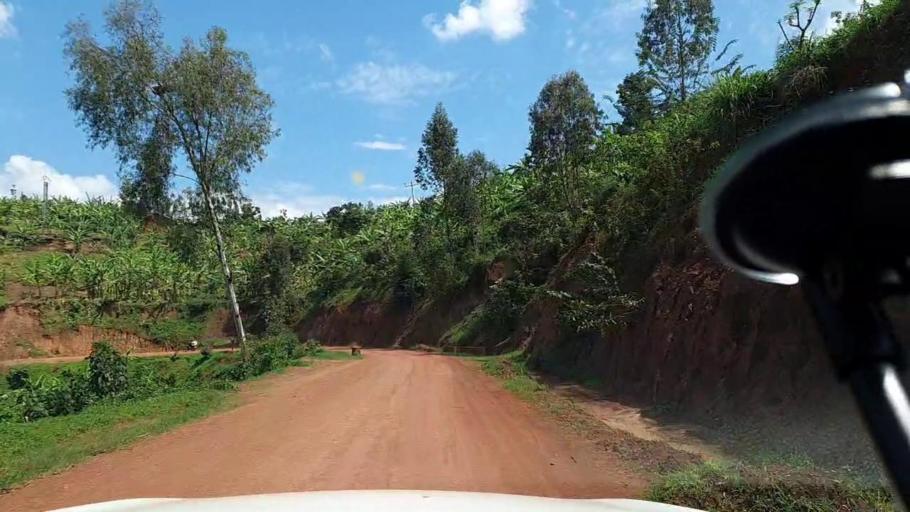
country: RW
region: Kigali
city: Kigali
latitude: -1.8018
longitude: 29.8937
